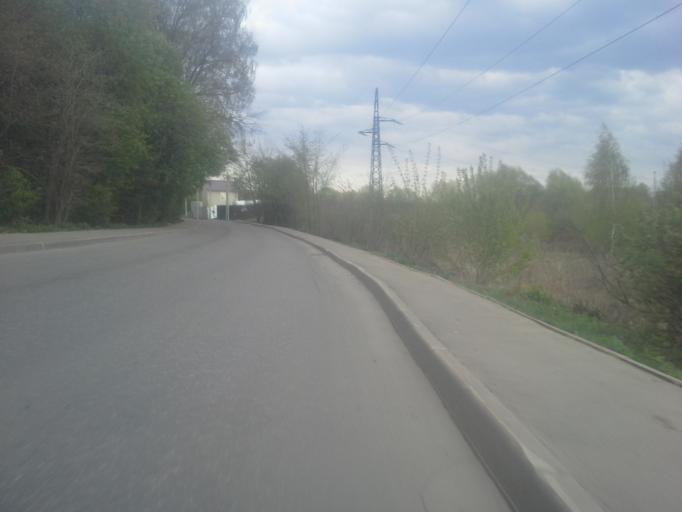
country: RU
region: Moskovskaya
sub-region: Leninskiy Rayon
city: Vnukovo
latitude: 55.6164
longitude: 37.3095
